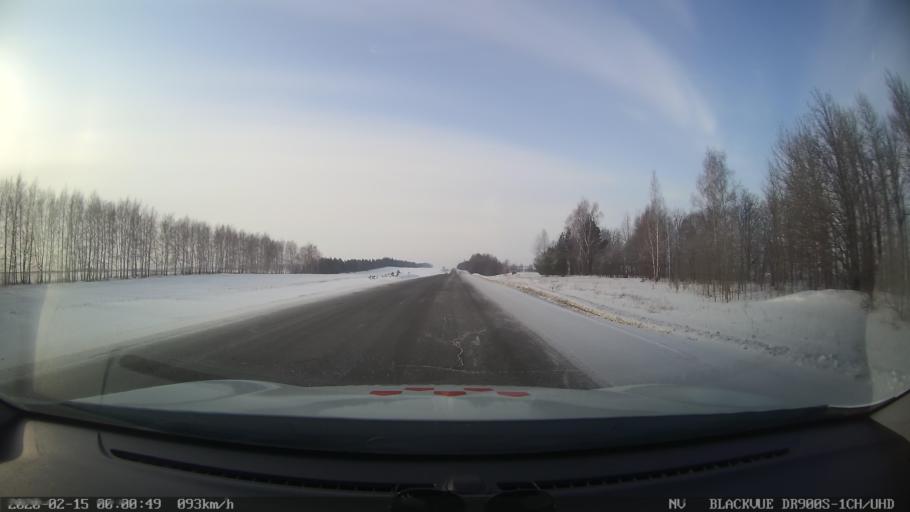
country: RU
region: Tatarstan
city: Kuybyshevskiy Zaton
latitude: 55.3442
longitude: 49.0298
